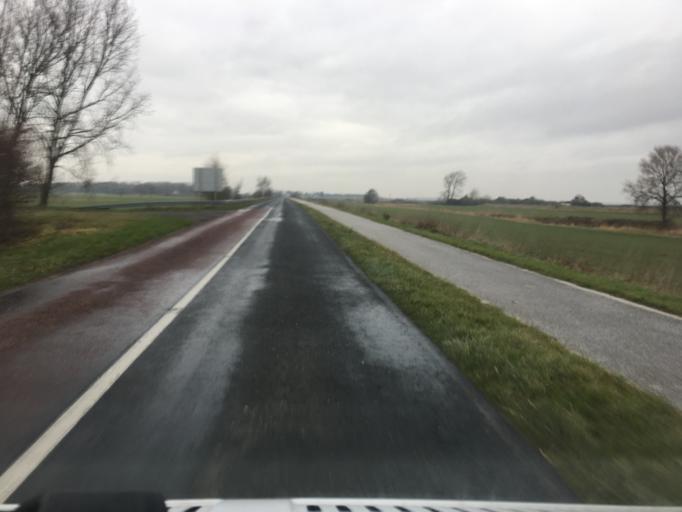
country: FR
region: Picardie
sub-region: Departement de la Somme
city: Pende
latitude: 50.2010
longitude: 1.5553
